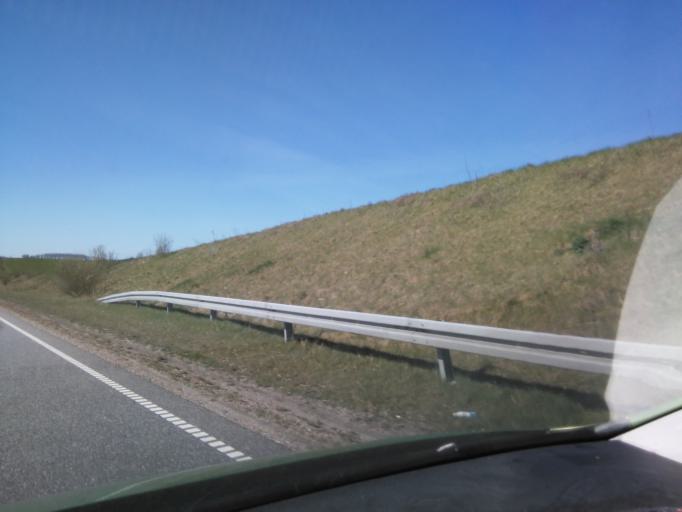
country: DK
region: South Denmark
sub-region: Vejle Kommune
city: Give
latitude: 55.8339
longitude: 9.2632
